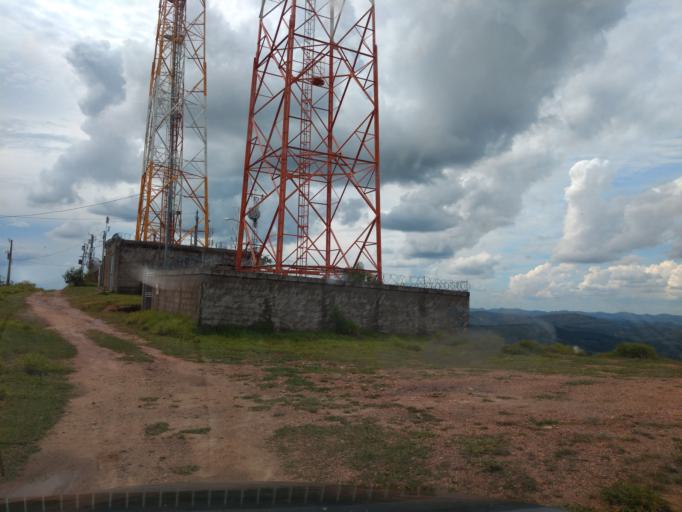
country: BR
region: Minas Gerais
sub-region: Lavras
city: Lavras
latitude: -21.5275
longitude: -44.9034
